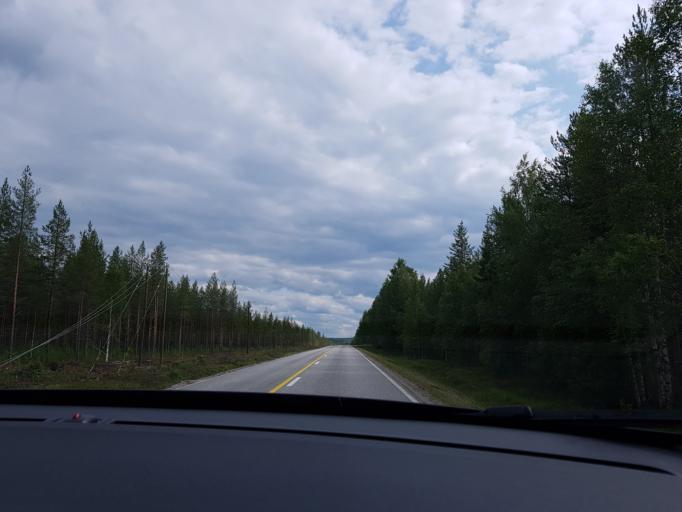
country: FI
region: Kainuu
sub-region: Kehys-Kainuu
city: Kuhmo
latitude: 64.3788
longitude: 29.8786
